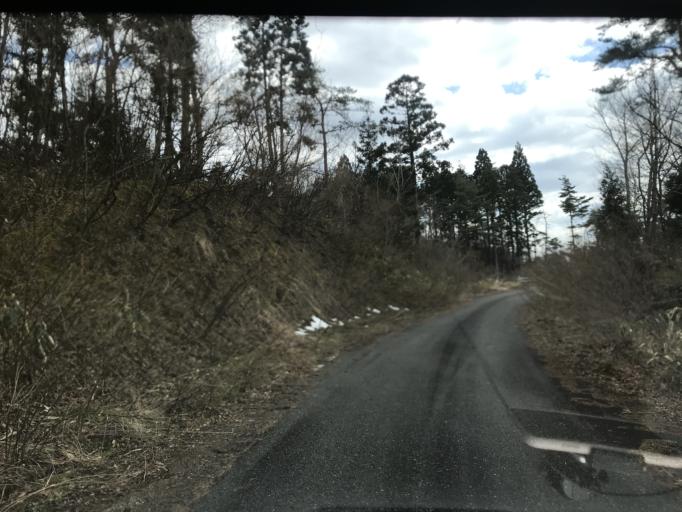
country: JP
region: Iwate
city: Ichinoseki
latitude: 38.9553
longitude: 141.0777
